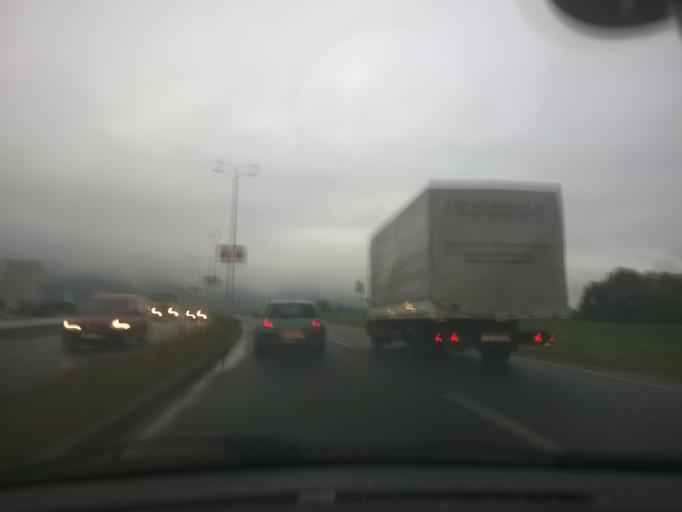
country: HR
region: Zagrebacka
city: Zapresic
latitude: 45.8714
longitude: 15.8217
